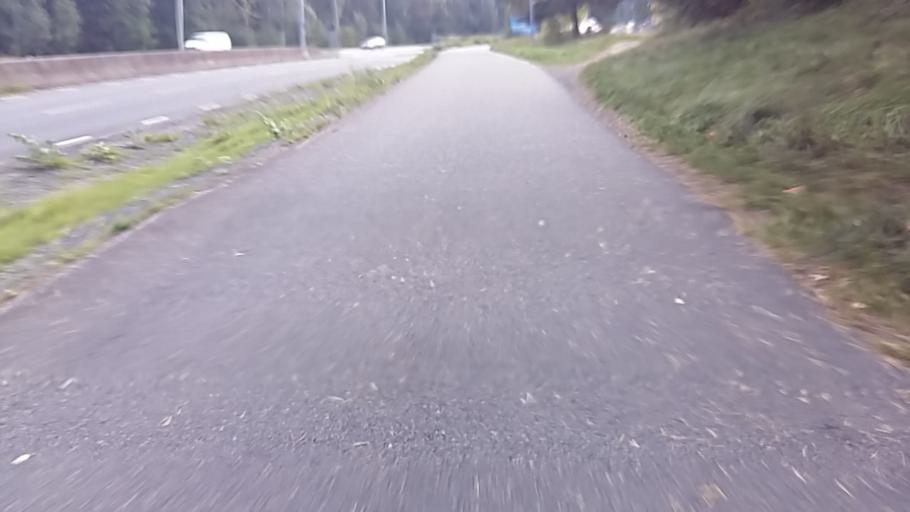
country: SE
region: Joenkoeping
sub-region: Jonkopings Kommun
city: Odensjo
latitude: 57.7467
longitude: 14.1563
